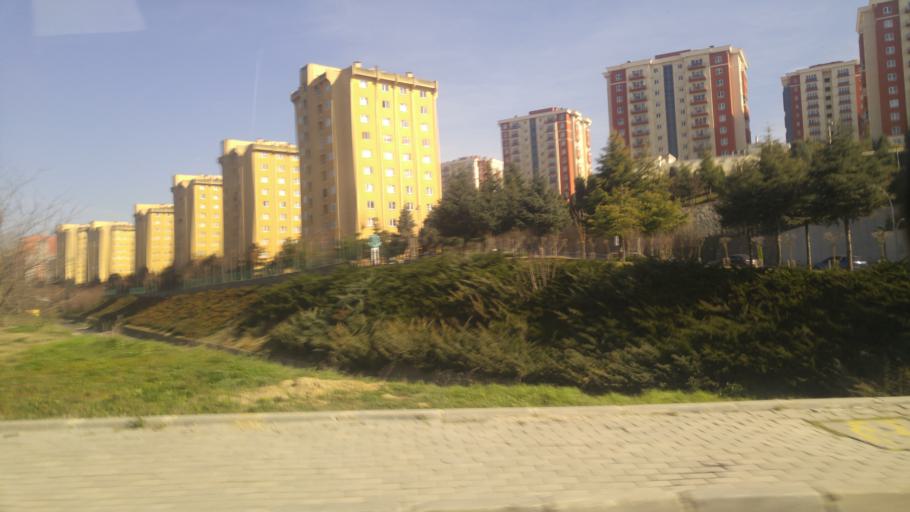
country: TR
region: Istanbul
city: Basaksehir
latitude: 41.0914
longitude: 28.8031
